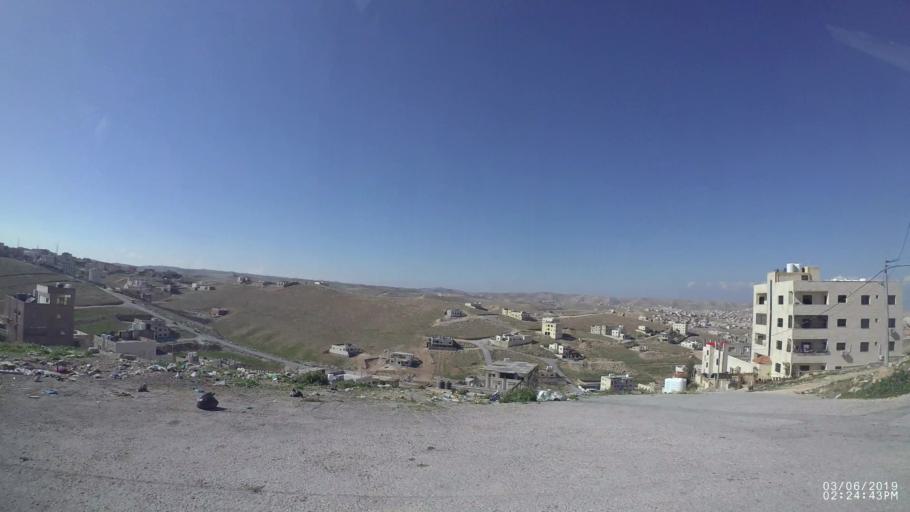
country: JO
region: Zarqa
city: Russeifa
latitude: 32.0423
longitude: 36.0383
